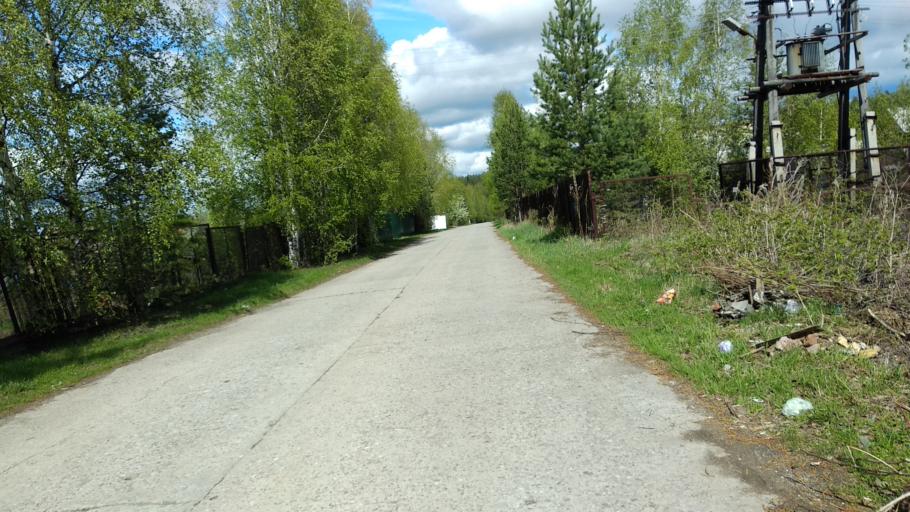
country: RU
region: Sverdlovsk
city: Krasnotur'insk
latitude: 59.8083
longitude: 60.1411
